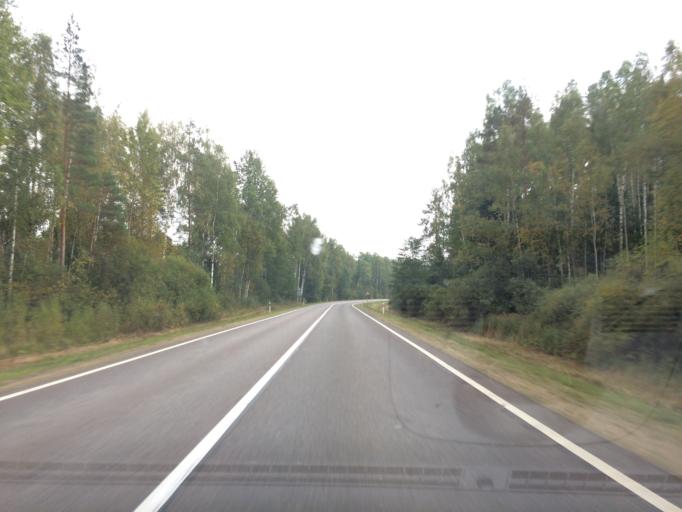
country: LV
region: Livani
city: Livani
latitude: 56.5361
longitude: 26.1361
